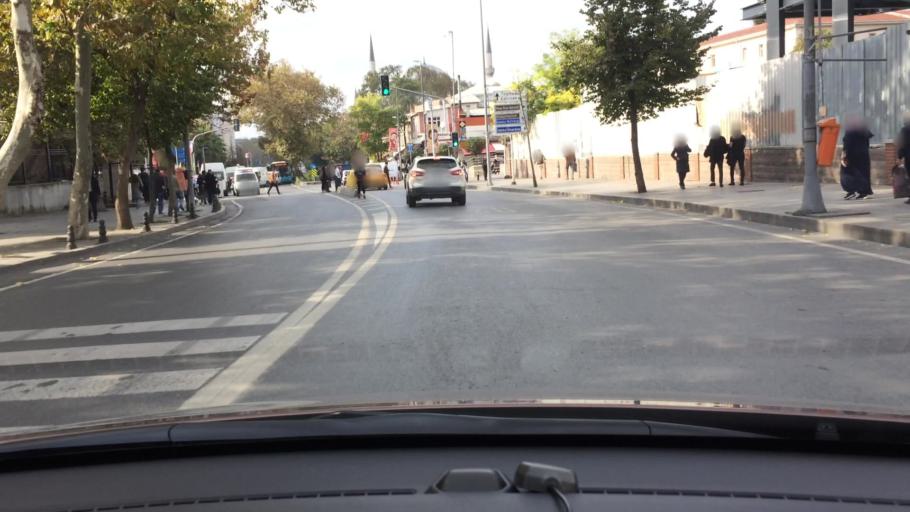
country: TR
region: Istanbul
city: Istanbul
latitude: 41.0119
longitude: 28.9601
